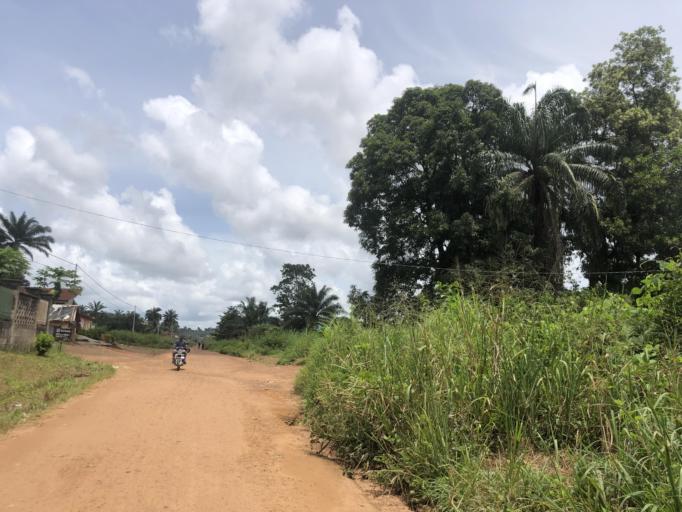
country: SL
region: Northern Province
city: Makeni
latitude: 8.8576
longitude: -12.0553
